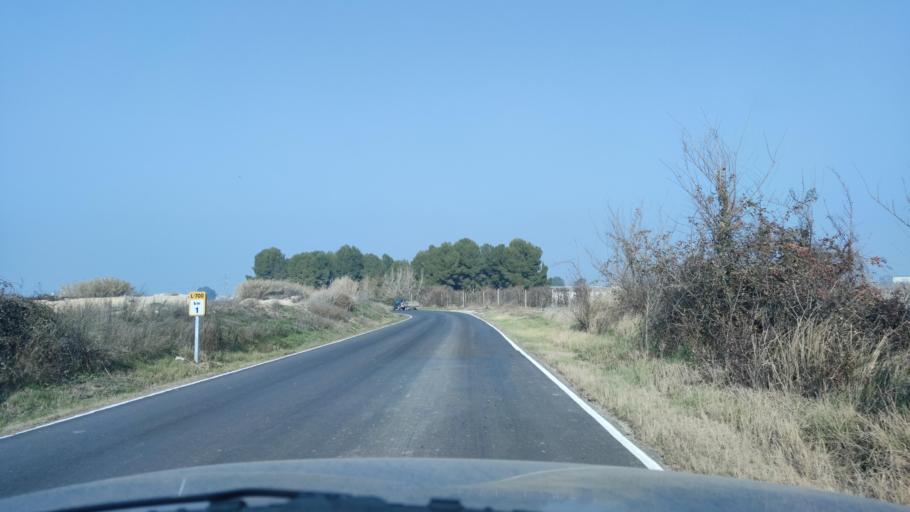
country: ES
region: Catalonia
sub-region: Provincia de Lleida
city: Alfes
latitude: 41.5659
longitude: 0.6123
